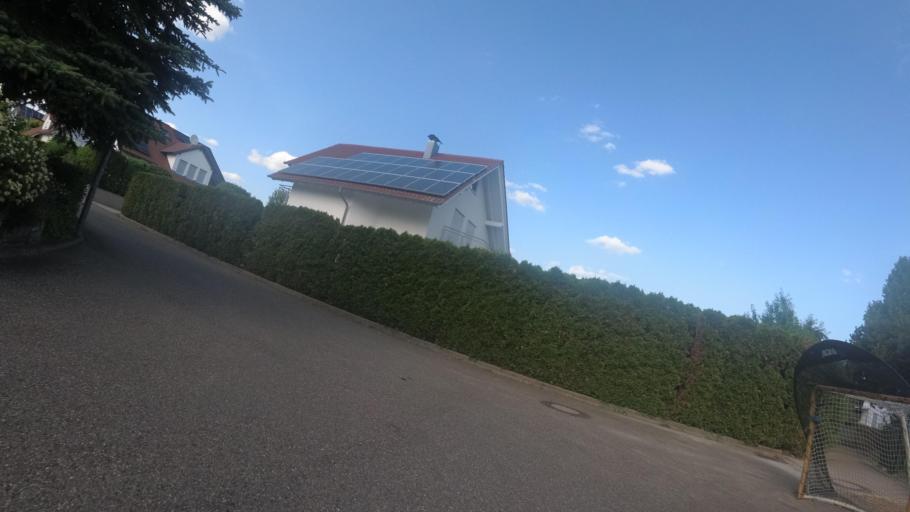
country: DE
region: Baden-Wuerttemberg
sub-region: Regierungsbezirk Stuttgart
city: Offenau
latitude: 49.2493
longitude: 9.1902
